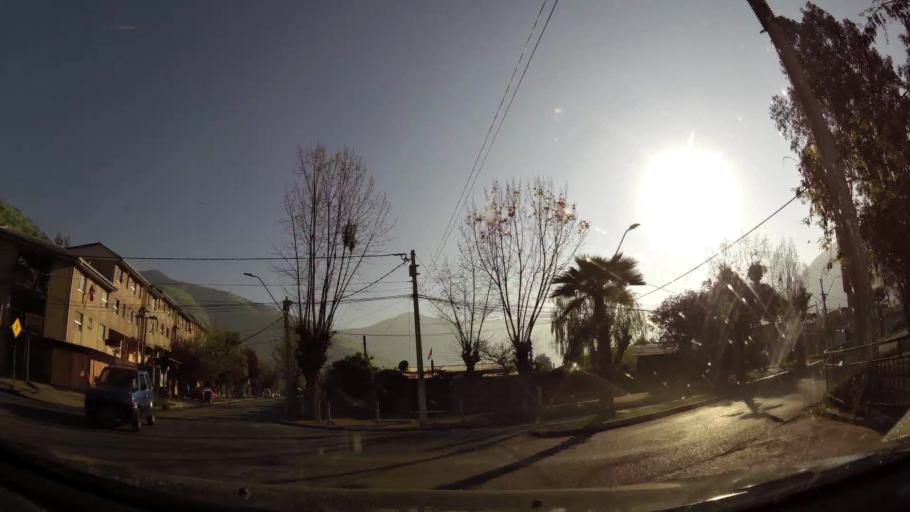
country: CL
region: Santiago Metropolitan
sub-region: Provincia de Chacabuco
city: Chicureo Abajo
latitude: -33.3684
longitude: -70.6400
